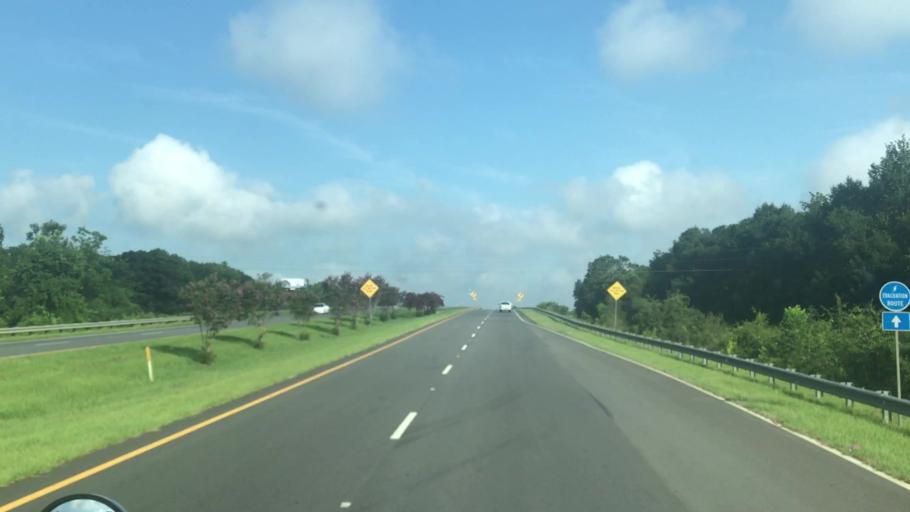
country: US
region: Georgia
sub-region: Decatur County
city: Bainbridge
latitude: 30.8953
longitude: -84.5826
